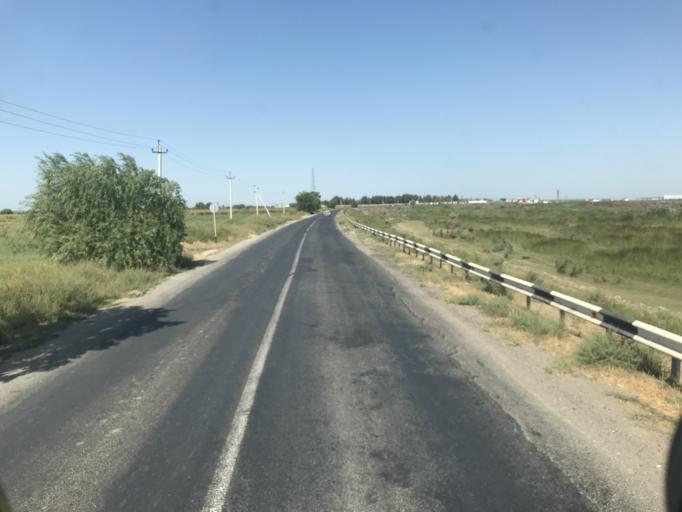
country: KZ
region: Ongtustik Qazaqstan
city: Ilyich
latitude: 40.9511
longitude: 68.4734
